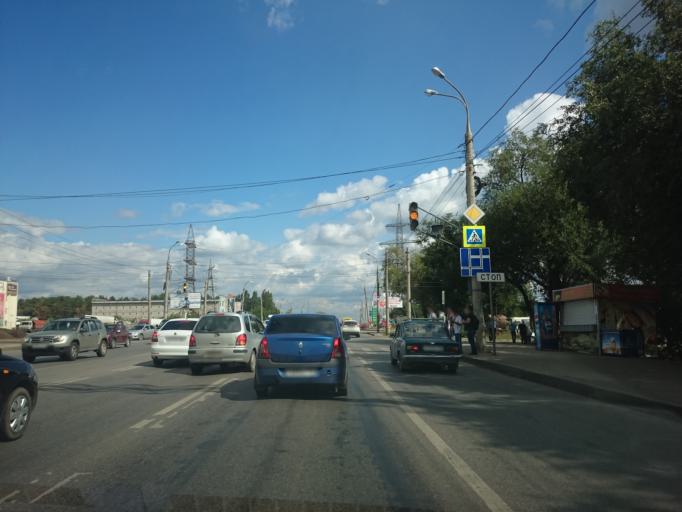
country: RU
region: Samara
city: Samara
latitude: 53.2606
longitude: 50.2383
